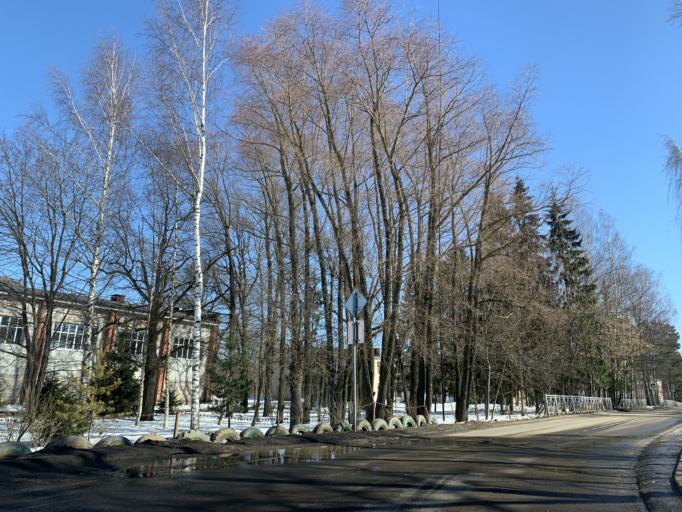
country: RU
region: Jaroslavl
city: Konstantinovskiy
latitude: 57.8421
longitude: 39.5771
